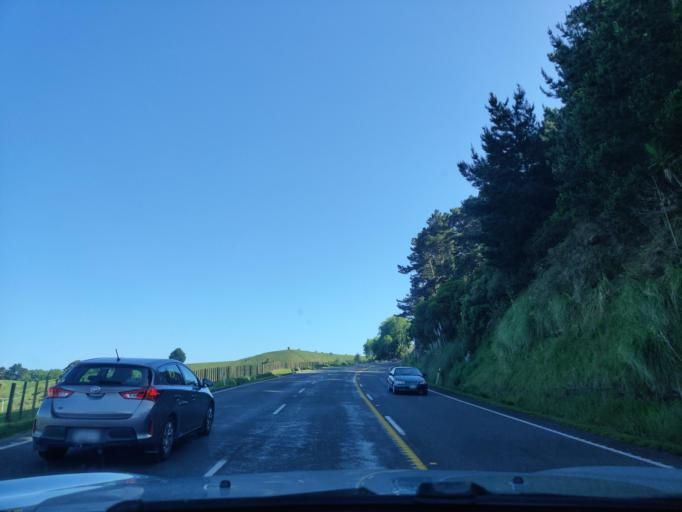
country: NZ
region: Manawatu-Wanganui
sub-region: Rangitikei District
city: Bulls
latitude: -40.0607
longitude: 175.2204
